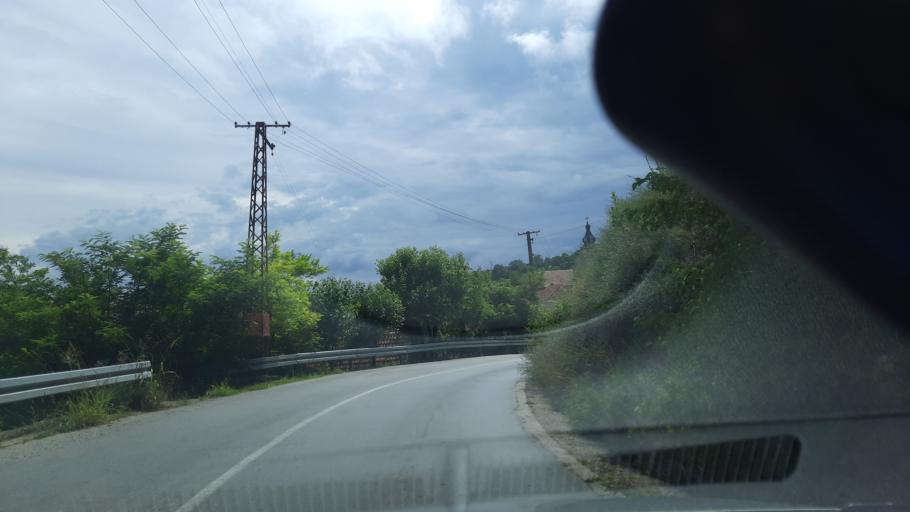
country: RS
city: Celarevo
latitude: 45.1258
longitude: 19.5726
